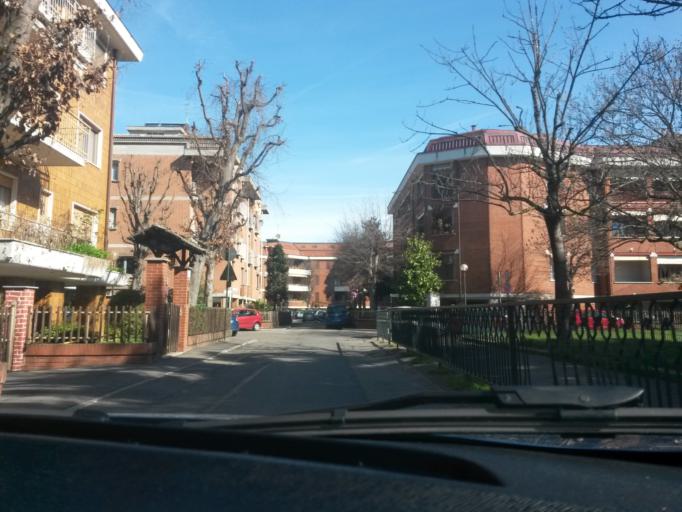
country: IT
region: Piedmont
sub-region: Provincia di Torino
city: Savonera
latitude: 45.0855
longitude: 7.6194
